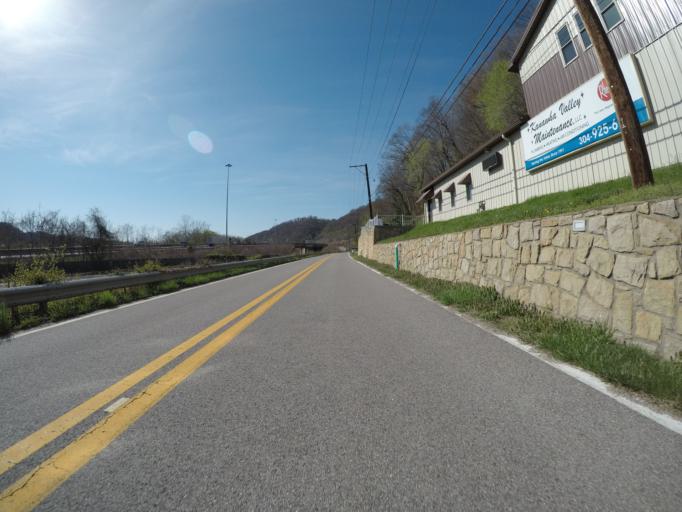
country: US
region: West Virginia
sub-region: Kanawha County
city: Rand
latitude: 38.3285
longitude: -81.5776
